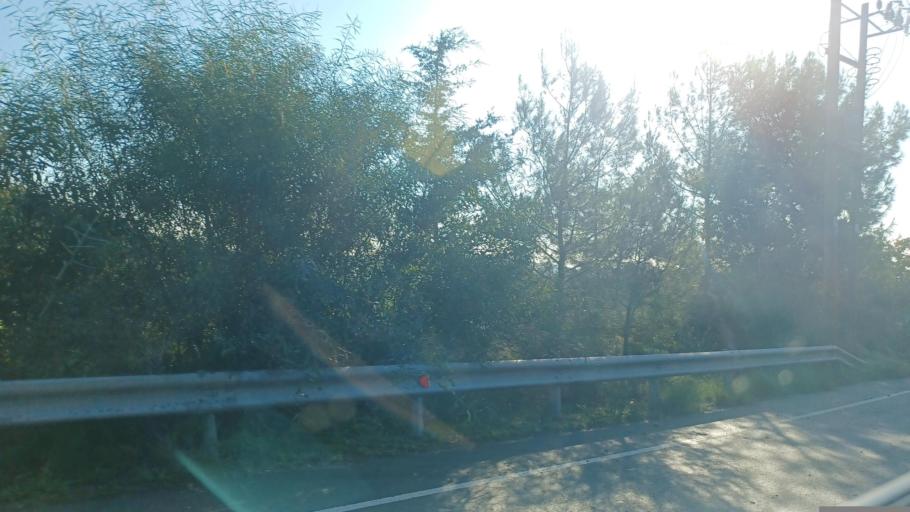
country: CY
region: Larnaka
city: Kofinou
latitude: 34.8459
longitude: 33.2997
